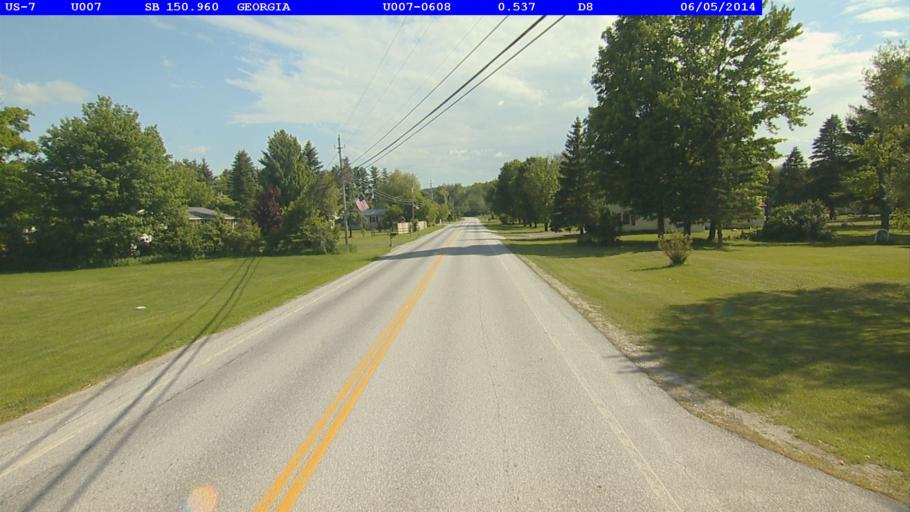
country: US
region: Vermont
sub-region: Chittenden County
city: Milton
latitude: 44.6868
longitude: -73.1102
